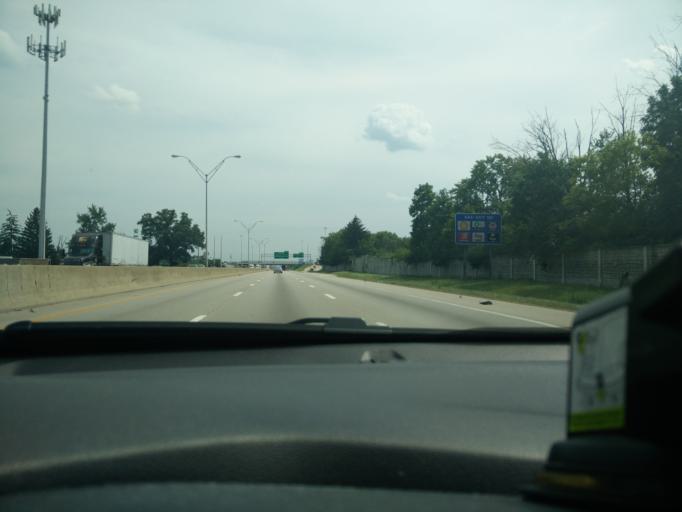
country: US
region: Ohio
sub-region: Montgomery County
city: Northridge
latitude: 39.8248
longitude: -84.1895
